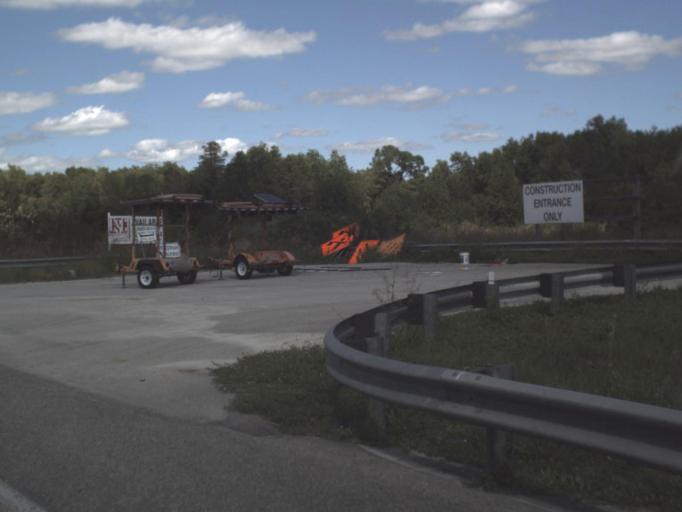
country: US
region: Florida
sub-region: Collier County
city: Lely Resort
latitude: 26.0616
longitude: -81.6963
